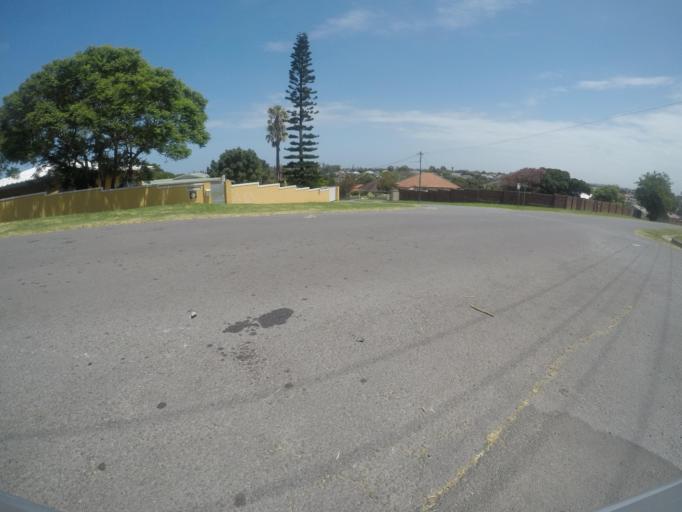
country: ZA
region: Eastern Cape
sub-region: Buffalo City Metropolitan Municipality
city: East London
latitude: -32.9759
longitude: 27.8794
